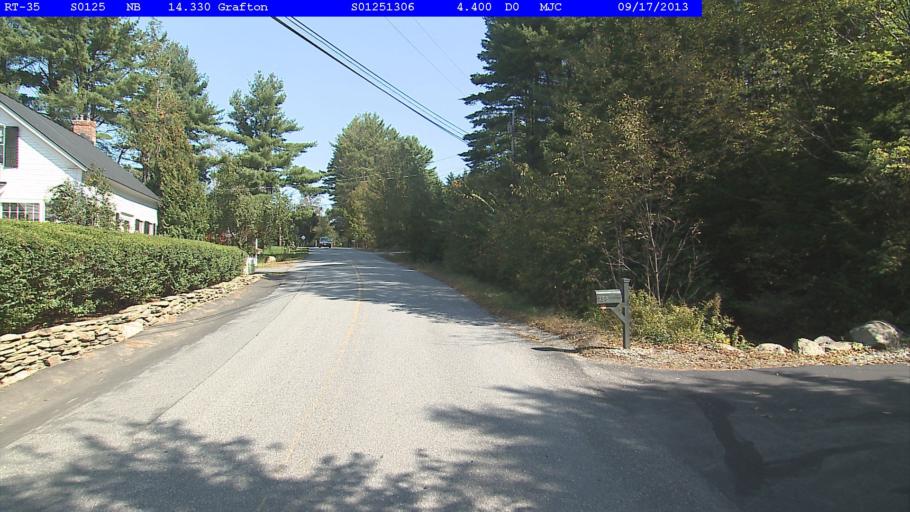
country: US
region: Vermont
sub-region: Windsor County
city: Chester
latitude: 43.1749
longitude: -72.6046
